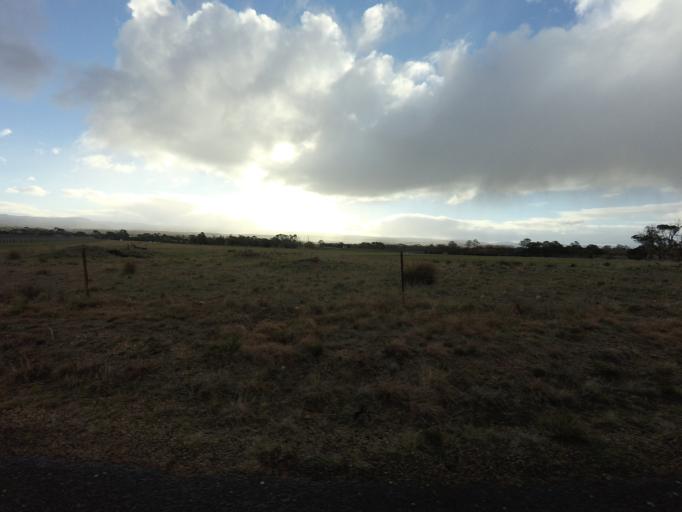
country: AU
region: Tasmania
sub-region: Break O'Day
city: St Helens
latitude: -42.0007
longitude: 148.0880
